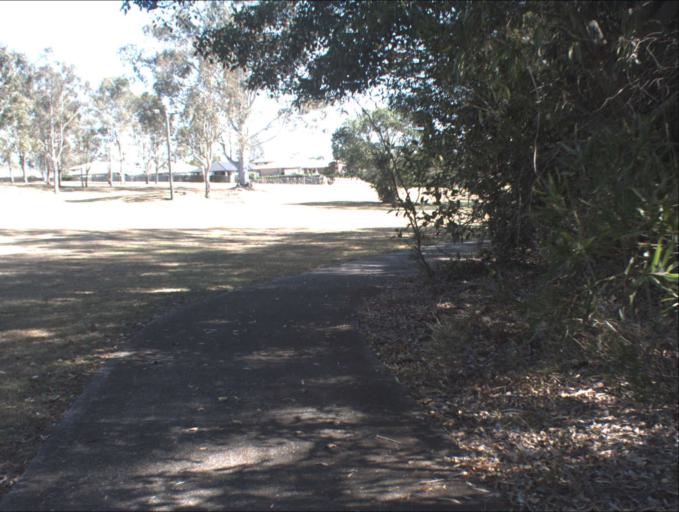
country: AU
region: Queensland
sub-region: Gold Coast
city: Yatala
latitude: -27.7083
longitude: 153.2277
